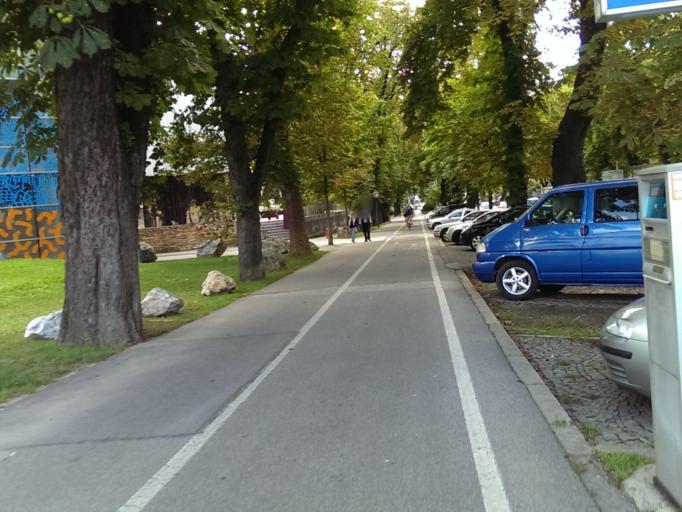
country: AT
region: Styria
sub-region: Graz Stadt
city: Graz
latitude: 47.0690
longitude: 15.4444
